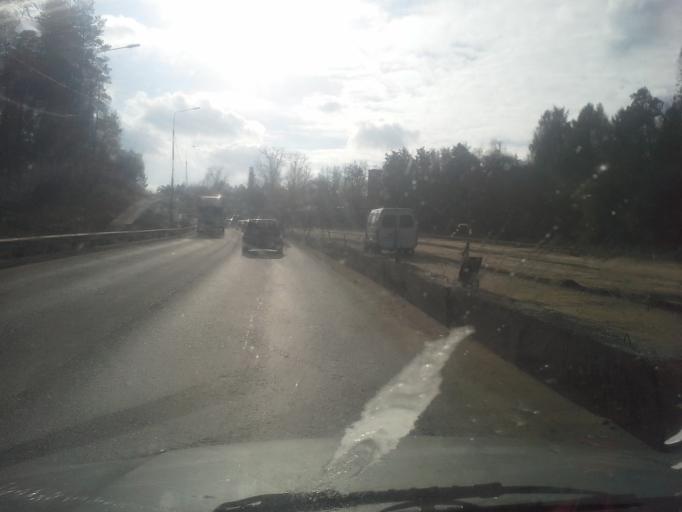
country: RU
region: Moskovskaya
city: Zvenigorod
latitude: 55.7090
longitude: 36.8744
